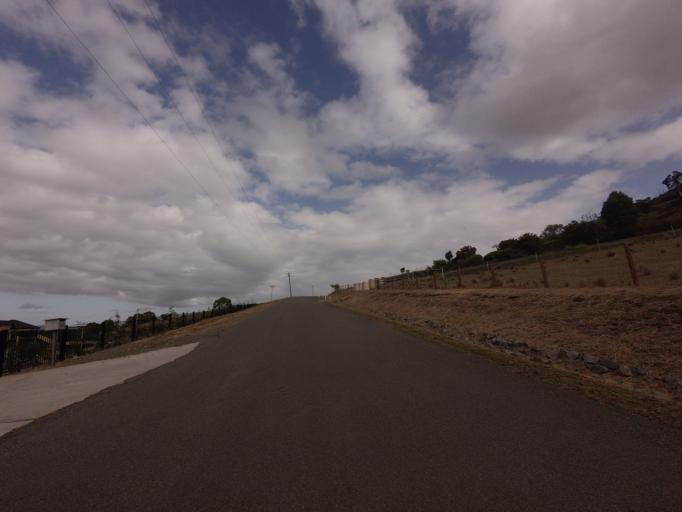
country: AU
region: Tasmania
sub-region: Clarence
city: Acton Park
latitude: -42.8582
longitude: 147.4662
